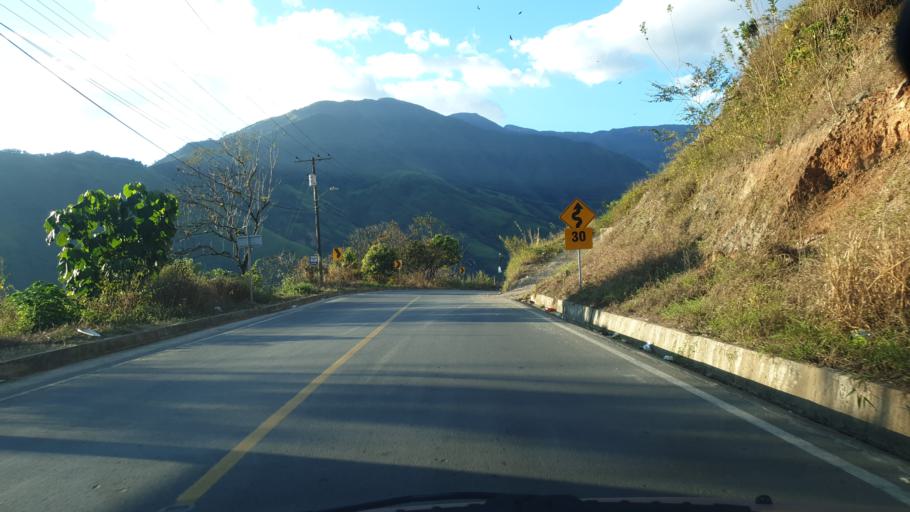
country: EC
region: El Oro
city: Zaruma
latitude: -3.6035
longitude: -79.6312
